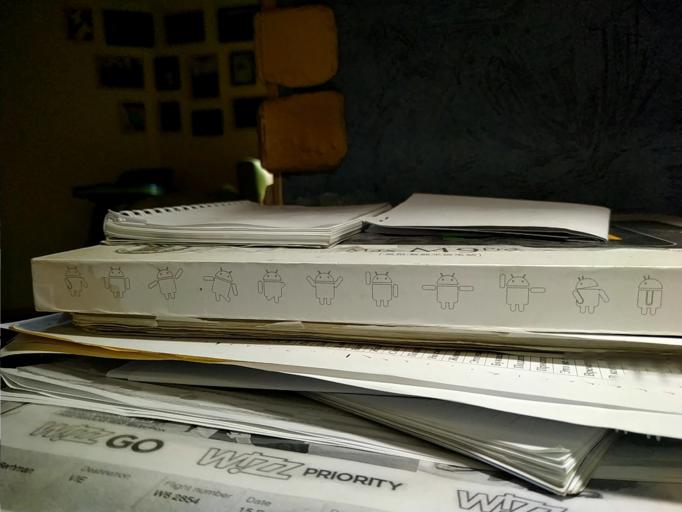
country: RU
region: Novgorod
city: Poddor'ye
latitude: 57.5287
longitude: 30.9060
